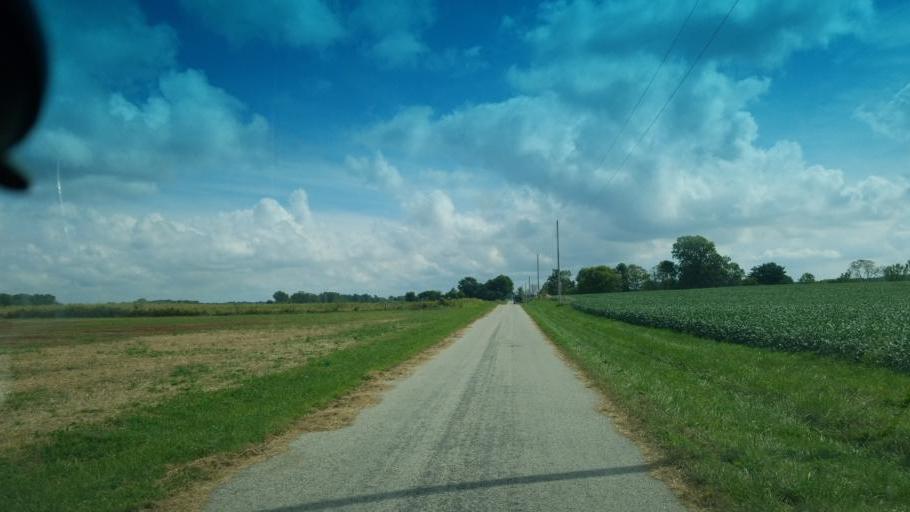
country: US
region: Ohio
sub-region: Seneca County
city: Tiffin
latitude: 40.9862
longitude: -83.1118
